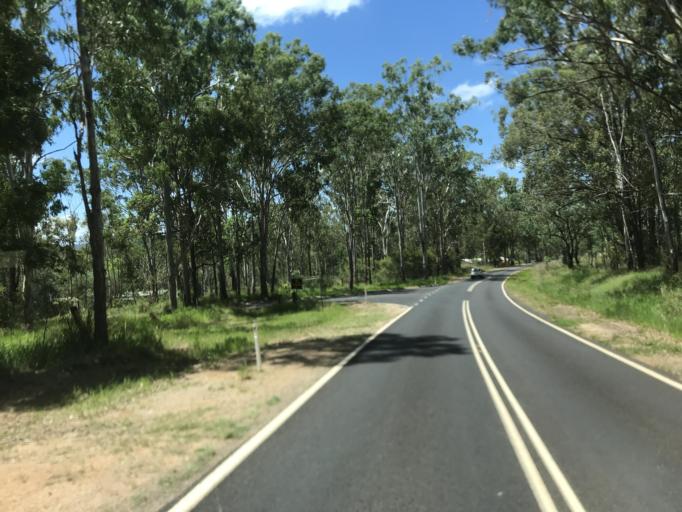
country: AU
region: Queensland
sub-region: Tablelands
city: Atherton
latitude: -17.4181
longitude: 145.3928
